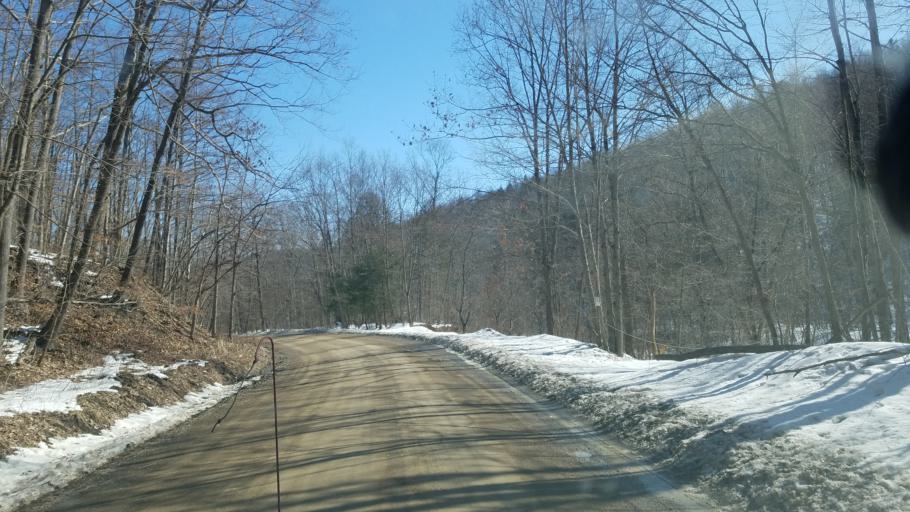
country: US
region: New York
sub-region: Allegany County
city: Alfred
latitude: 42.2479
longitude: -77.7071
